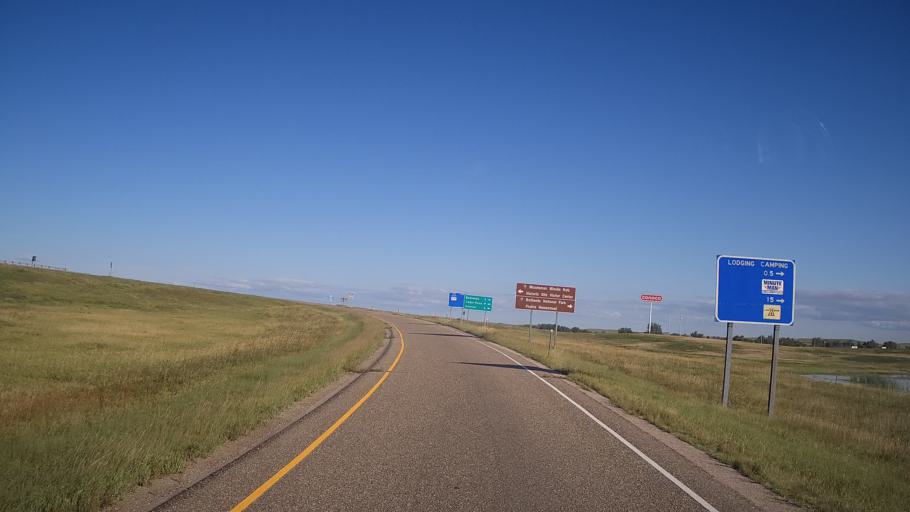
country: US
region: South Dakota
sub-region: Haakon County
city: Philip
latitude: 43.8405
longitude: -101.9019
